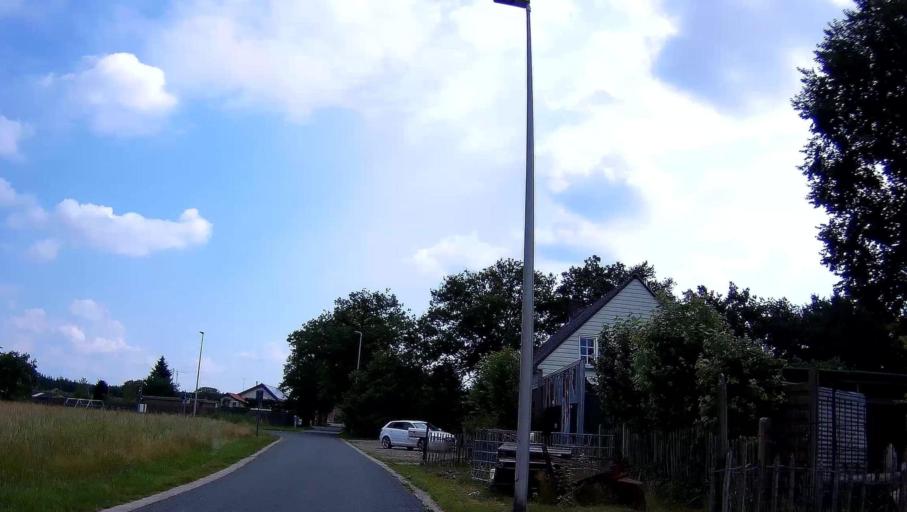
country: BE
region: Flanders
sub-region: Provincie Limburg
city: Lommel
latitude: 51.2190
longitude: 5.2477
